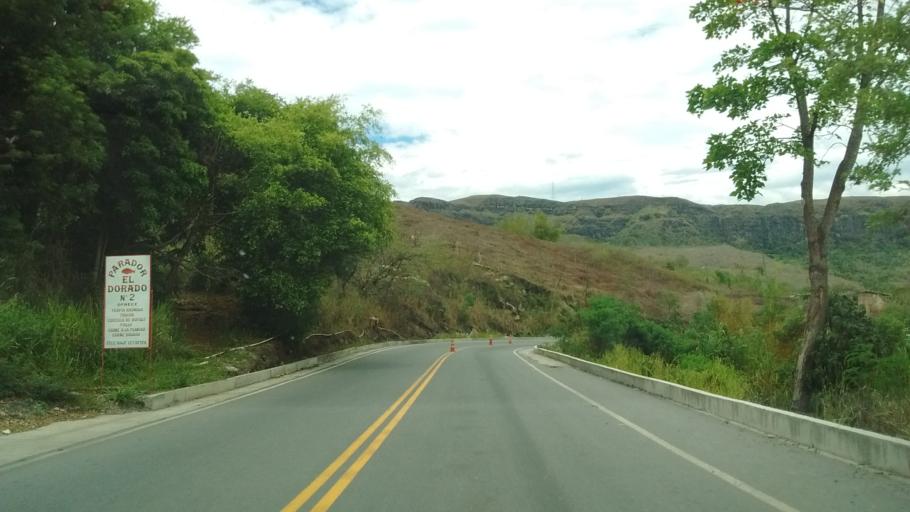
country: CO
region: Cauca
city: La Sierra
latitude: 2.2019
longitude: -76.8158
